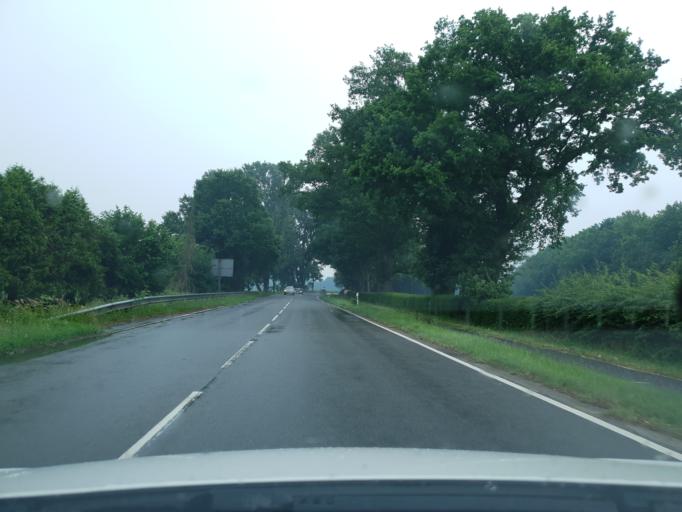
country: DE
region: Lower Saxony
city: Lingen
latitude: 52.5406
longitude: 7.2946
